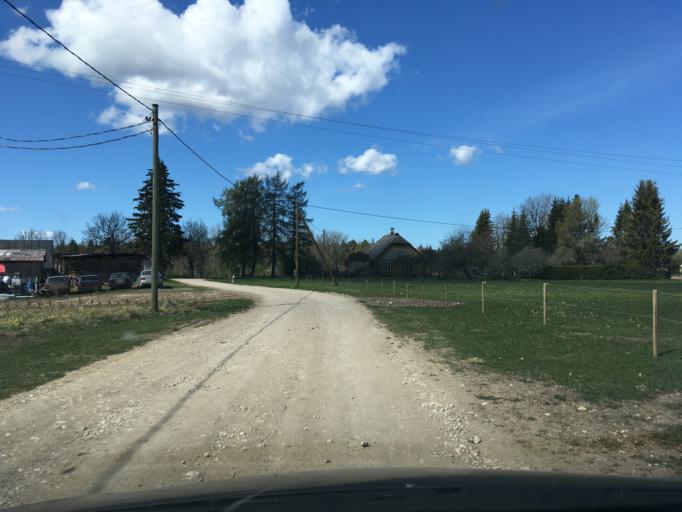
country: EE
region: Harju
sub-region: Raasiku vald
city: Raasiku
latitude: 59.2163
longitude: 25.1602
